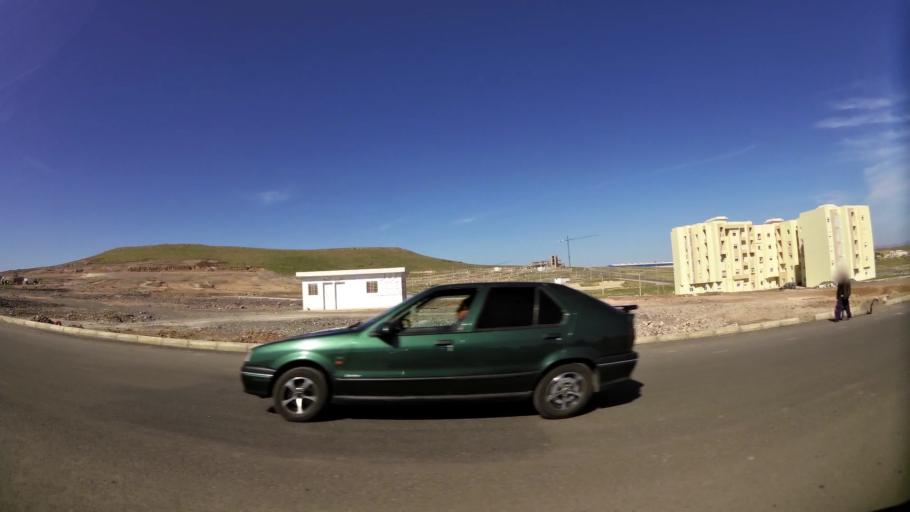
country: MA
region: Oriental
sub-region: Oujda-Angad
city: Oujda
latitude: 34.6501
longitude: -1.9535
